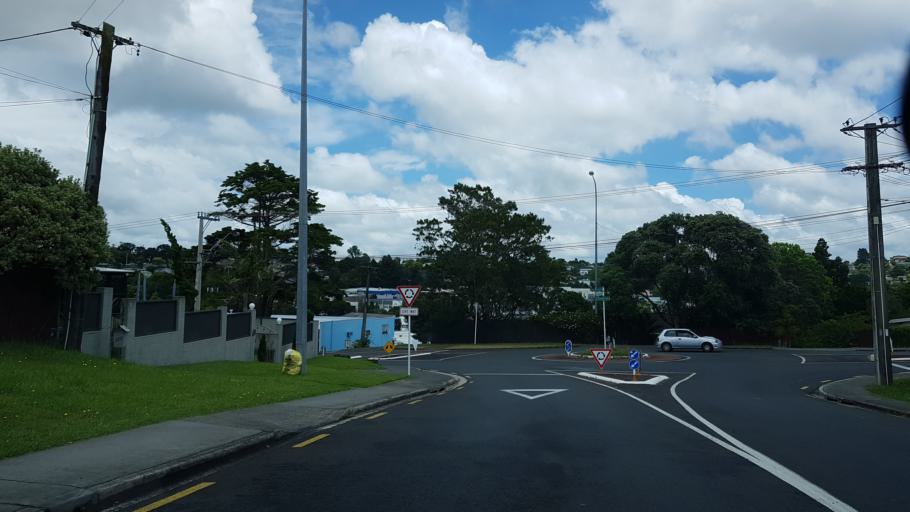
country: NZ
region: Auckland
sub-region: Auckland
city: North Shore
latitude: -36.7646
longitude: 174.7337
